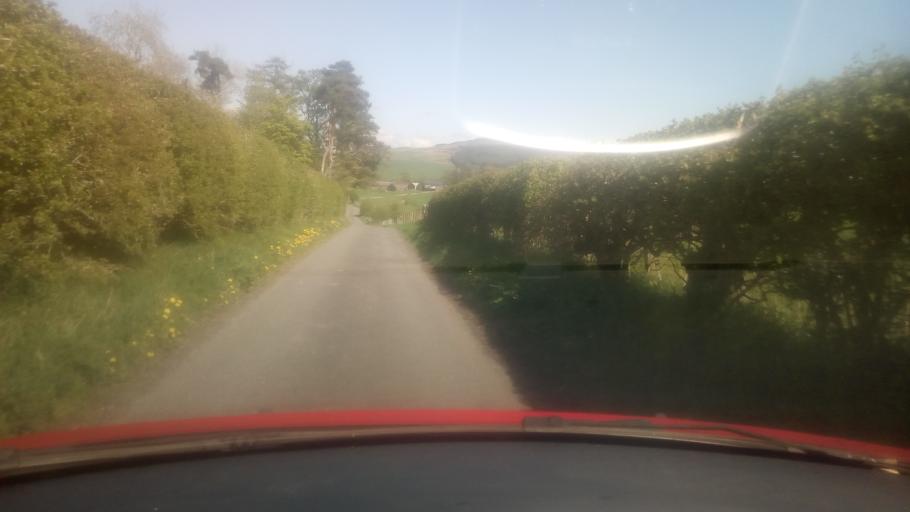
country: GB
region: Scotland
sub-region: The Scottish Borders
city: Hawick
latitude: 55.4214
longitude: -2.7155
